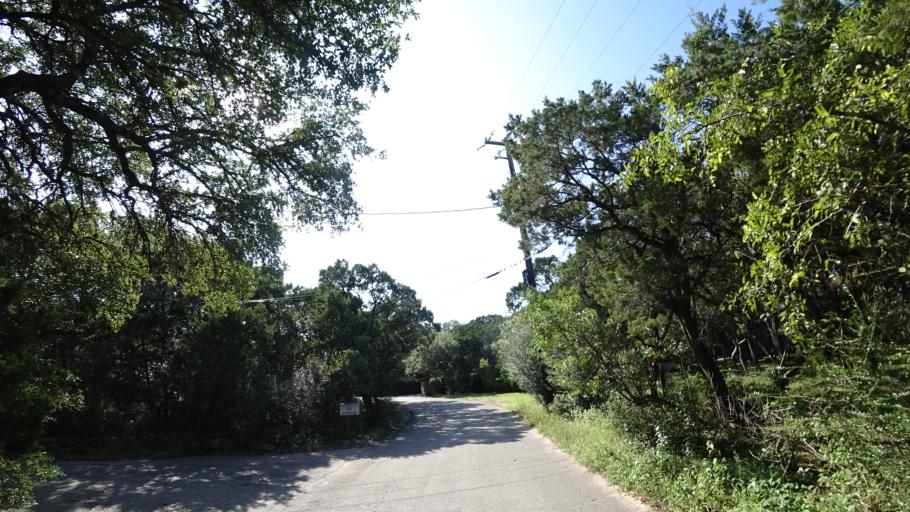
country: US
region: Texas
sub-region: Travis County
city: West Lake Hills
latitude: 30.2903
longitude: -97.8115
